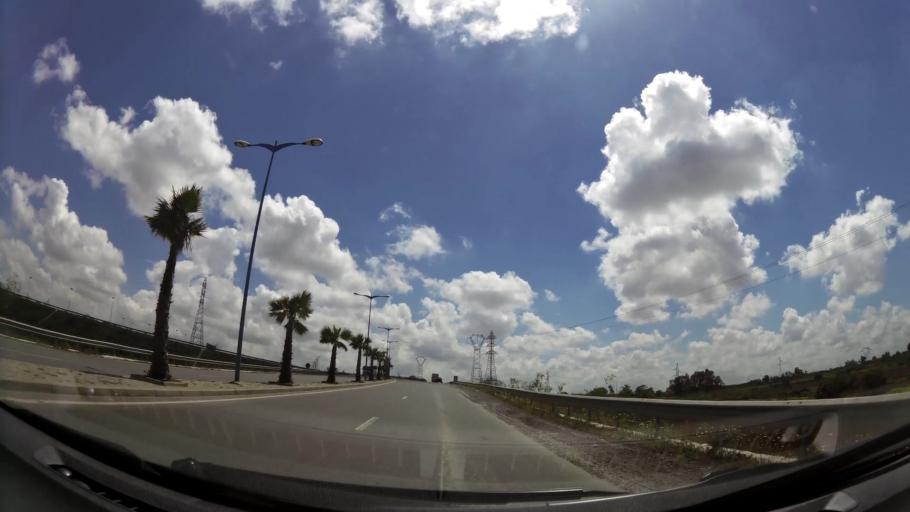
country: MA
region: Grand Casablanca
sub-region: Nouaceur
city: Bouskoura
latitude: 33.5121
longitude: -7.6132
